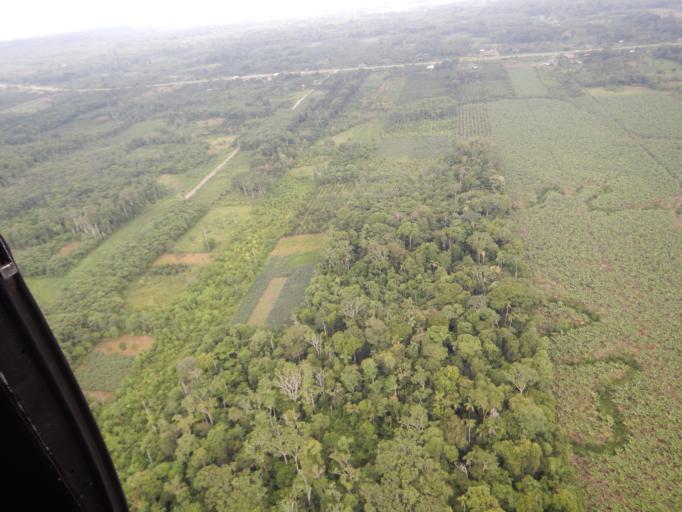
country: BO
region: Cochabamba
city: Chimore
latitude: -17.1089
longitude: -64.8197
